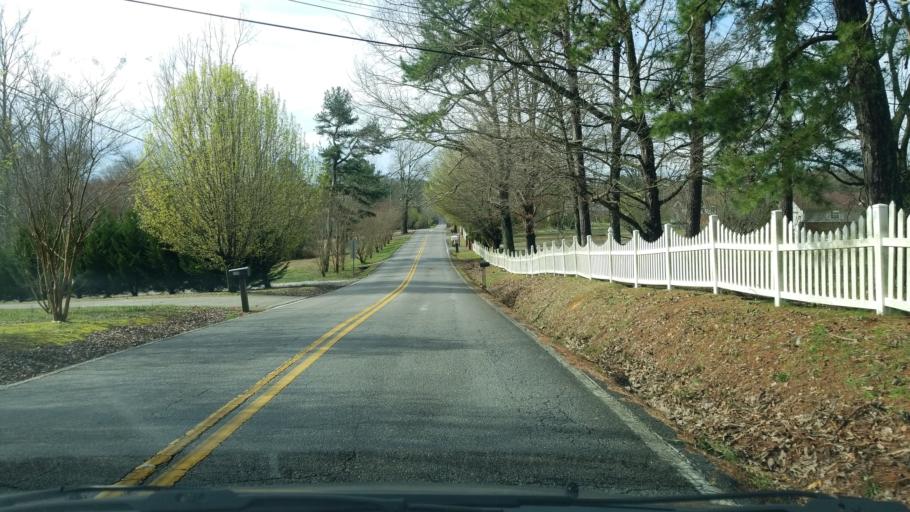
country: US
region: Tennessee
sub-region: Hamilton County
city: Collegedale
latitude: 35.0550
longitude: -85.1000
